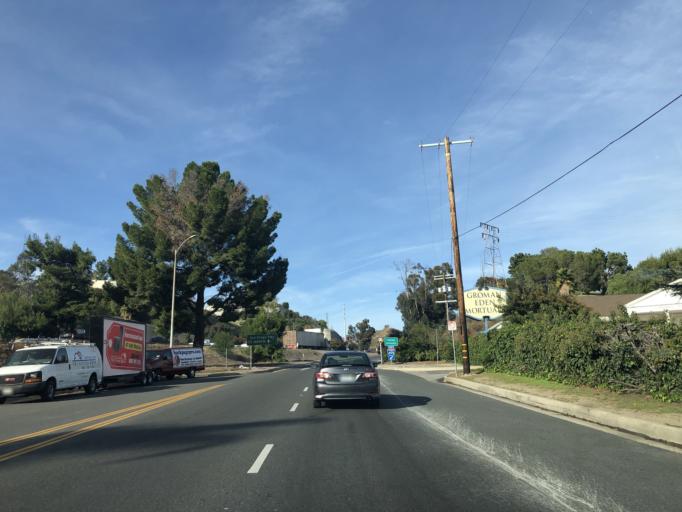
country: US
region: California
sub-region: Los Angeles County
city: San Fernando
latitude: 34.2797
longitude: -118.4690
